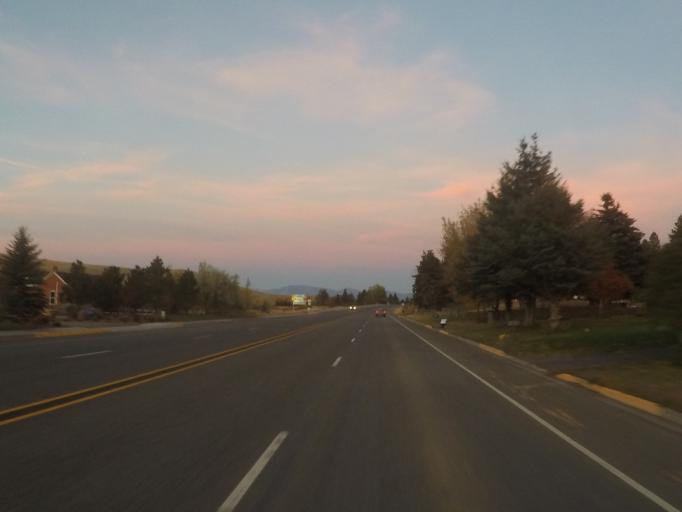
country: US
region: Montana
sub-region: Lewis and Clark County
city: Helena West Side
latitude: 46.5966
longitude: -112.1067
